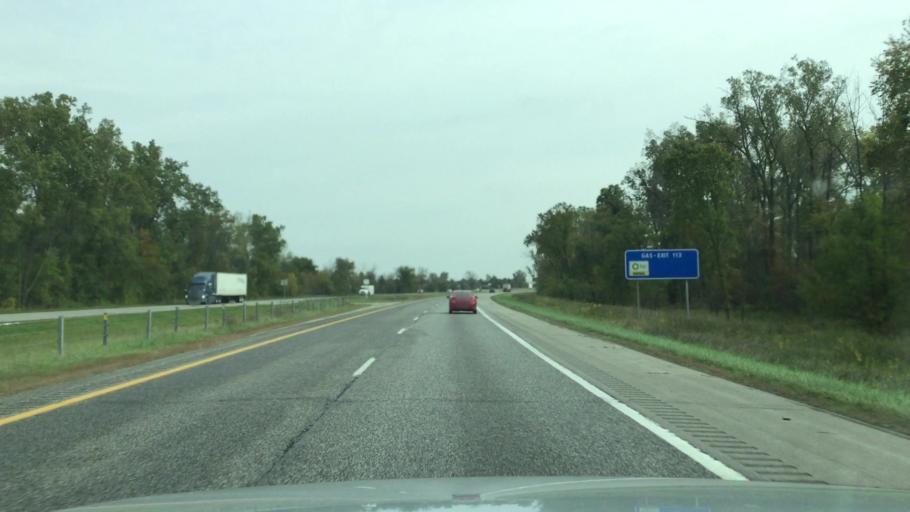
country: US
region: Michigan
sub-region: Shiawassee County
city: Corunna
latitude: 42.8893
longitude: -84.1061
